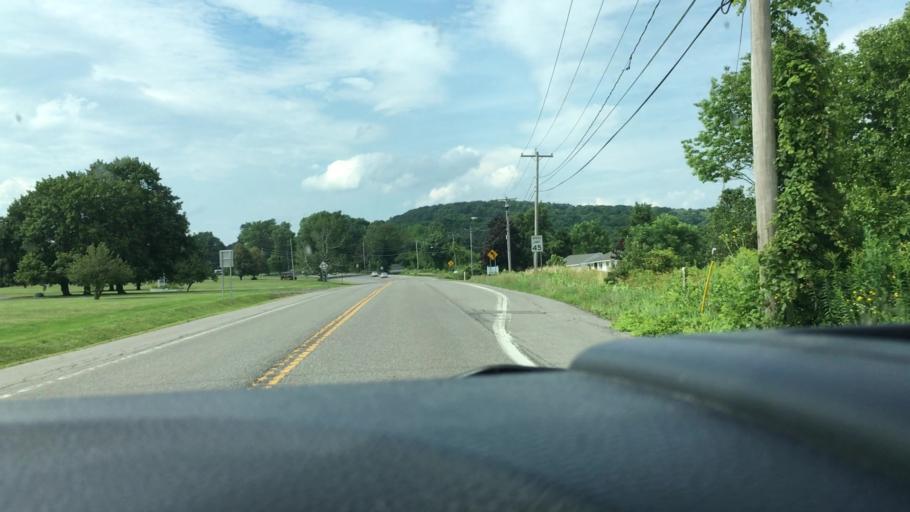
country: US
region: New York
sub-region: Onondaga County
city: Nedrow
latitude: 42.8876
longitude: -76.0951
